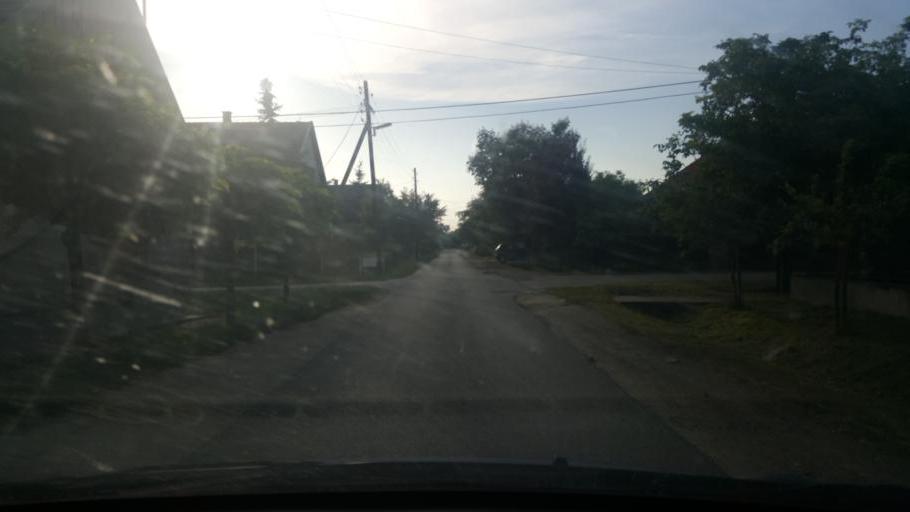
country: HU
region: Pest
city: Monor
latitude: 47.3379
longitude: 19.4492
